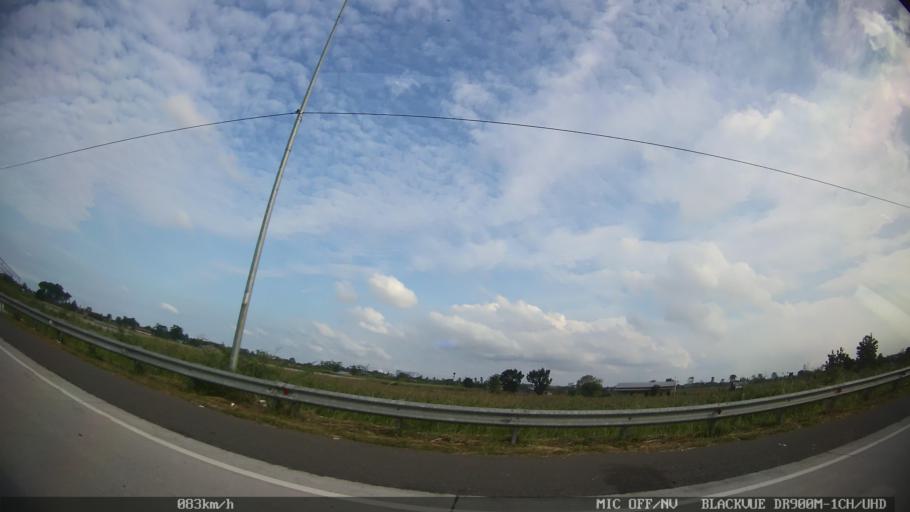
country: ID
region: North Sumatra
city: Medan
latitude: 3.6391
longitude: 98.6439
